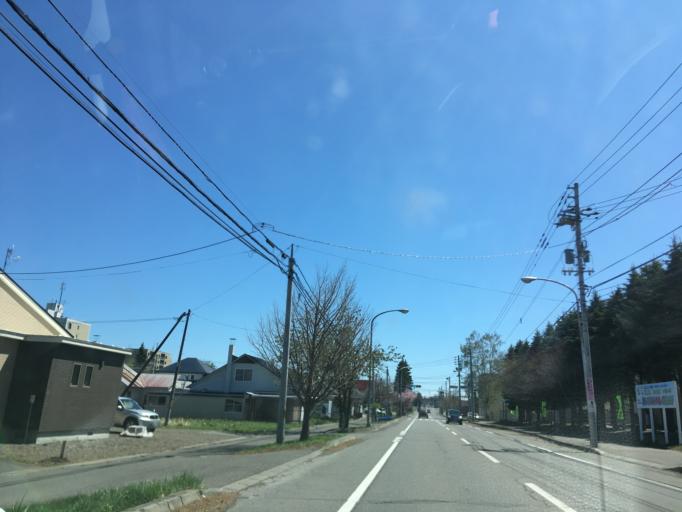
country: JP
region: Hokkaido
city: Obihiro
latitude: 42.9227
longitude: 143.1712
